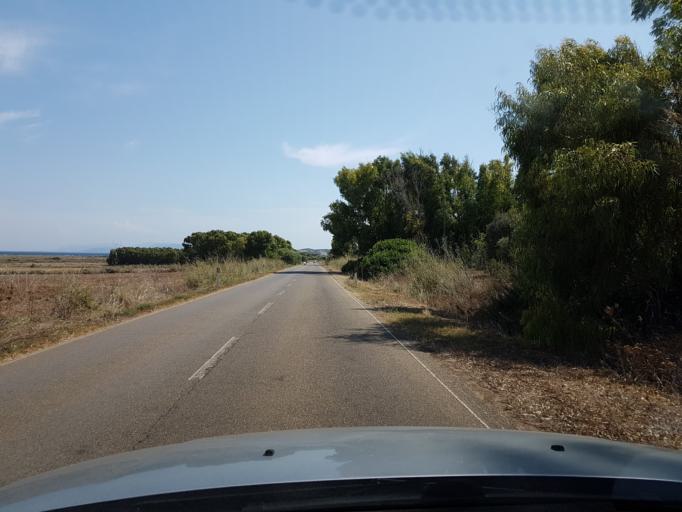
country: IT
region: Sardinia
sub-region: Provincia di Oristano
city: Cabras
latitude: 39.8948
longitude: 8.4348
